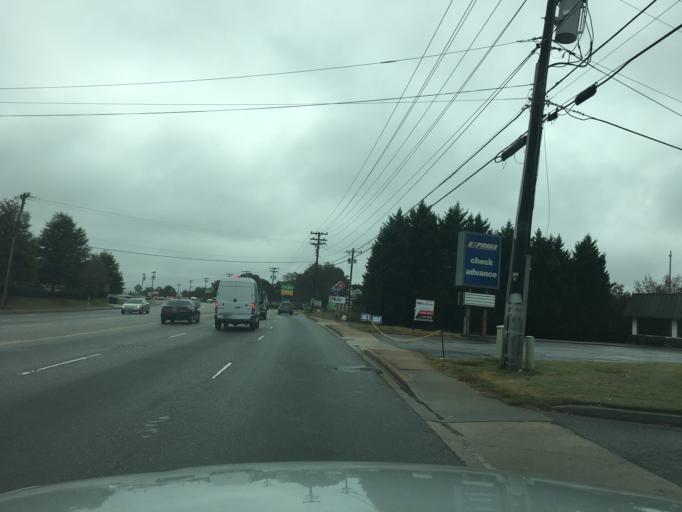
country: US
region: South Carolina
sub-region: Greenville County
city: Welcome
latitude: 34.8138
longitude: -82.4409
